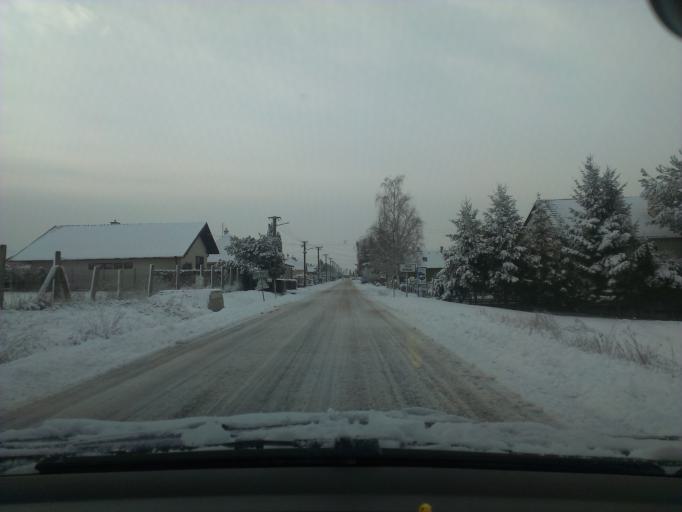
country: SK
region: Trnavsky
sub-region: Okres Trnava
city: Piestany
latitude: 48.5108
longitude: 17.9838
